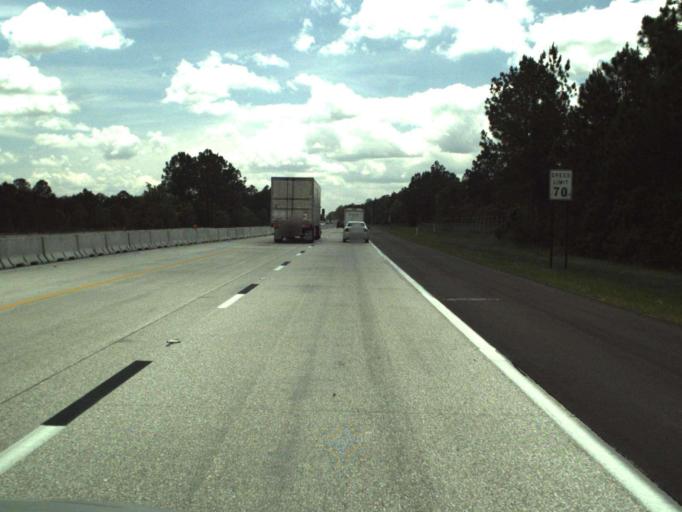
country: US
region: Florida
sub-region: Volusia County
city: Lake Helen
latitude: 29.0684
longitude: -81.1840
